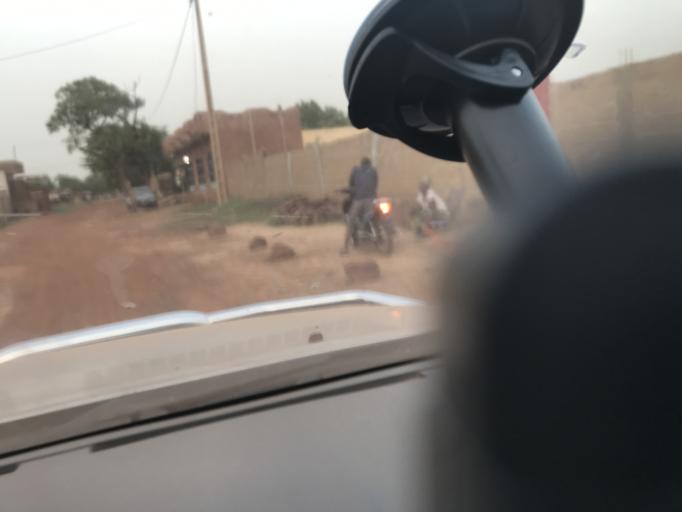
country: ML
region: Bamako
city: Bamako
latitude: 12.6528
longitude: -7.8904
